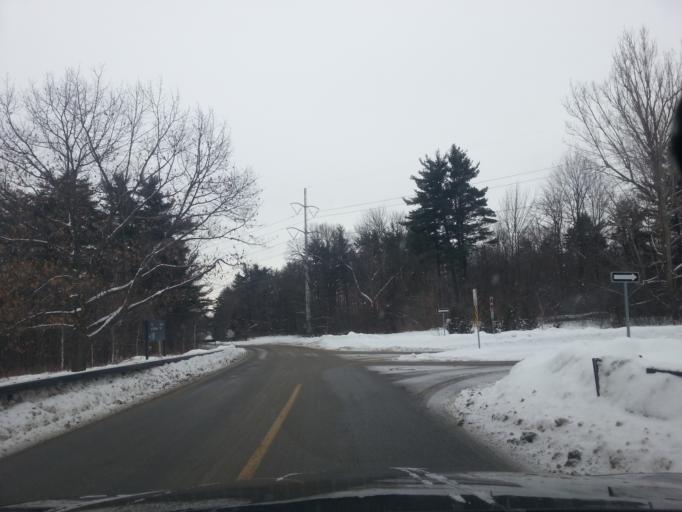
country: CA
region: Ontario
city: Ottawa
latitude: 45.4320
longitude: -75.7500
